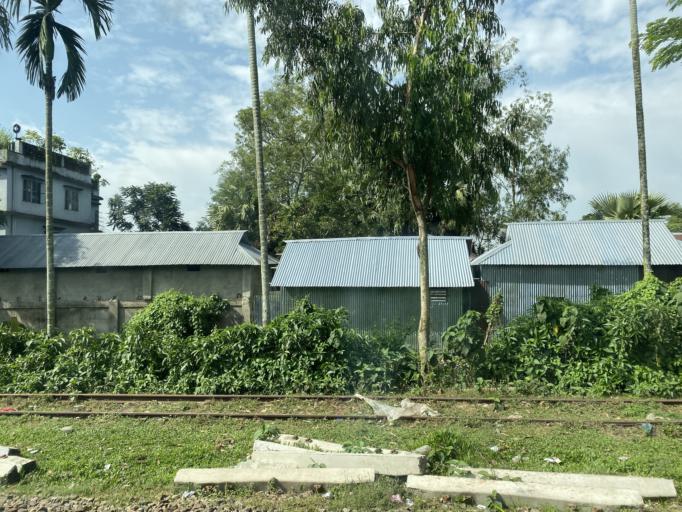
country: BD
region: Sylhet
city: Habiganj
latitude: 24.1795
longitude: 91.3569
